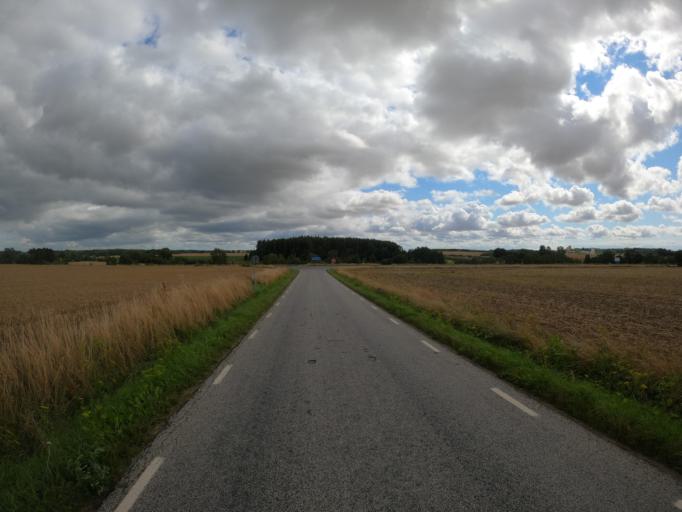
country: SE
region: Skane
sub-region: Lunds Kommun
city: Lund
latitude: 55.7157
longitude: 13.3026
